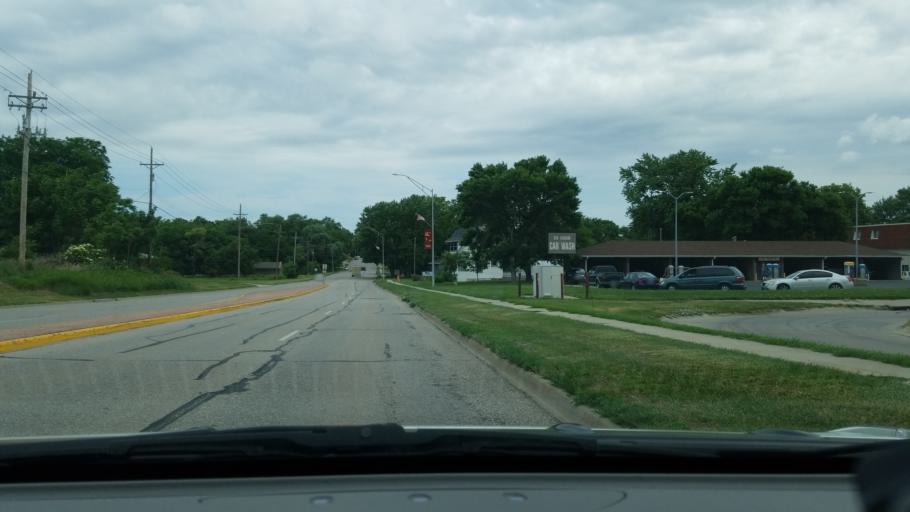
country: US
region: Nebraska
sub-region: Sarpy County
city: Papillion
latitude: 41.1440
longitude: -96.0428
